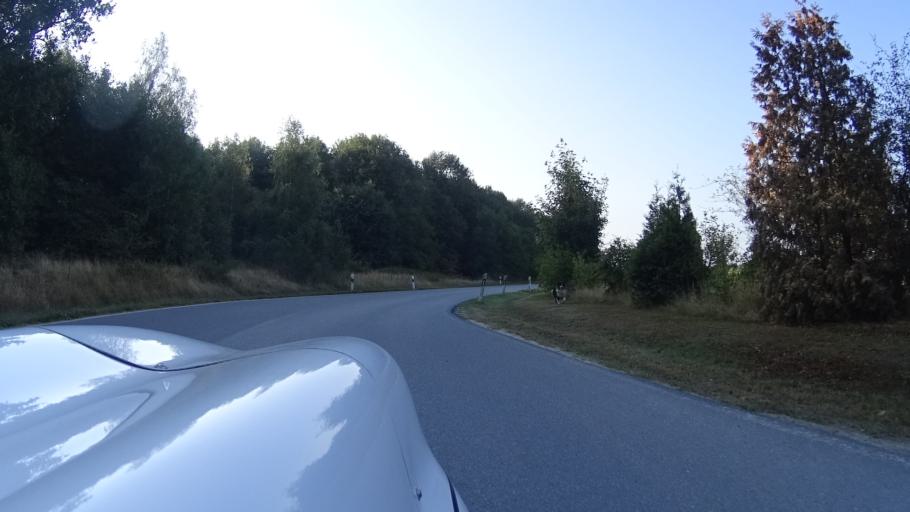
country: DE
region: North Rhine-Westphalia
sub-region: Regierungsbezirk Dusseldorf
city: Kevelaer
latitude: 51.5539
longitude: 6.2018
